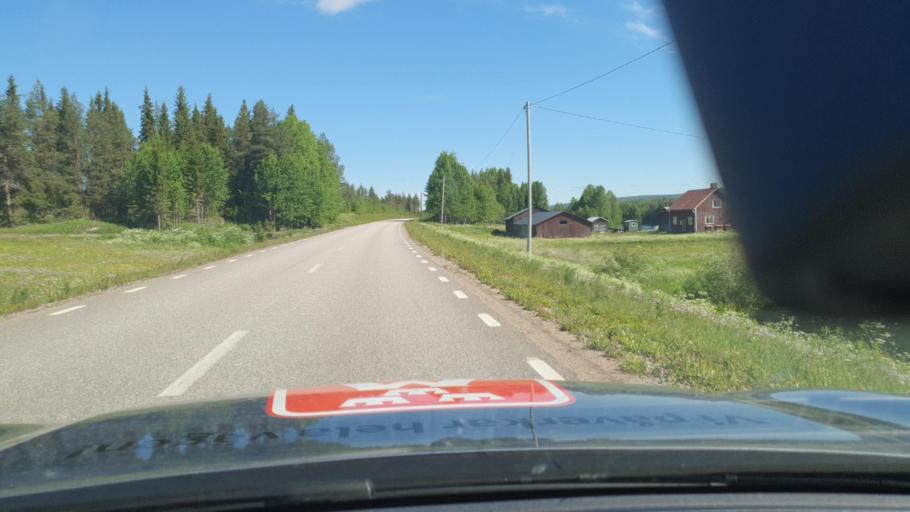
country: SE
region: Norrbotten
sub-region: Overkalix Kommun
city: OEverkalix
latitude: 66.7643
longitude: 22.6834
